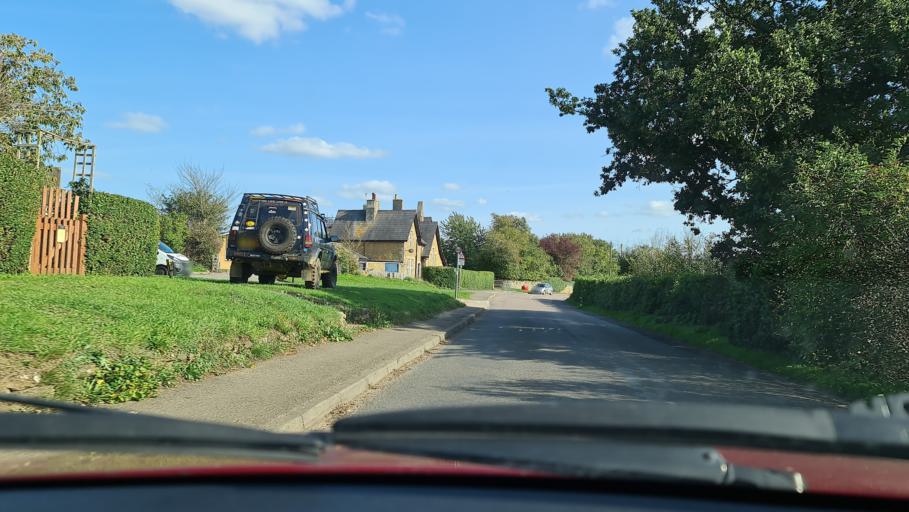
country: GB
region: England
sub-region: Oxfordshire
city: Adderbury
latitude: 52.0217
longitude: -1.2331
